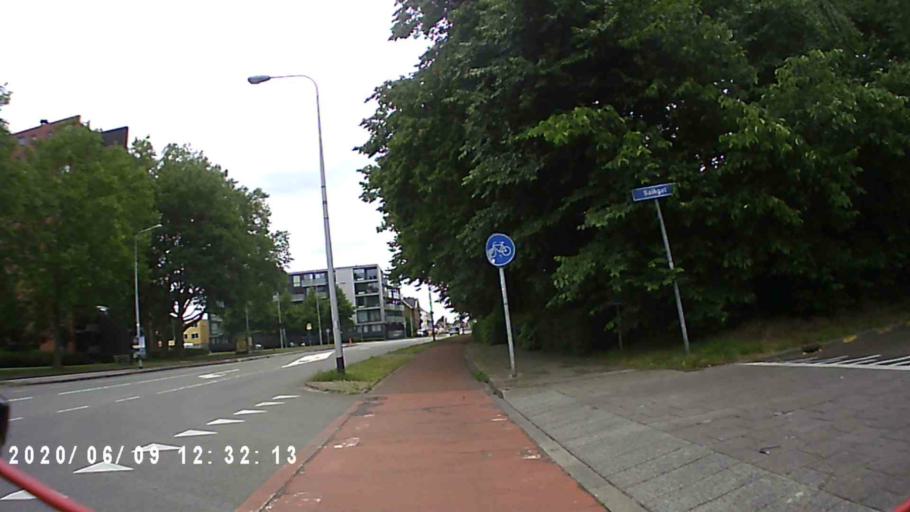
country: NL
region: Groningen
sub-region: Gemeente Groningen
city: Oosterpark
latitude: 53.2201
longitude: 6.5824
